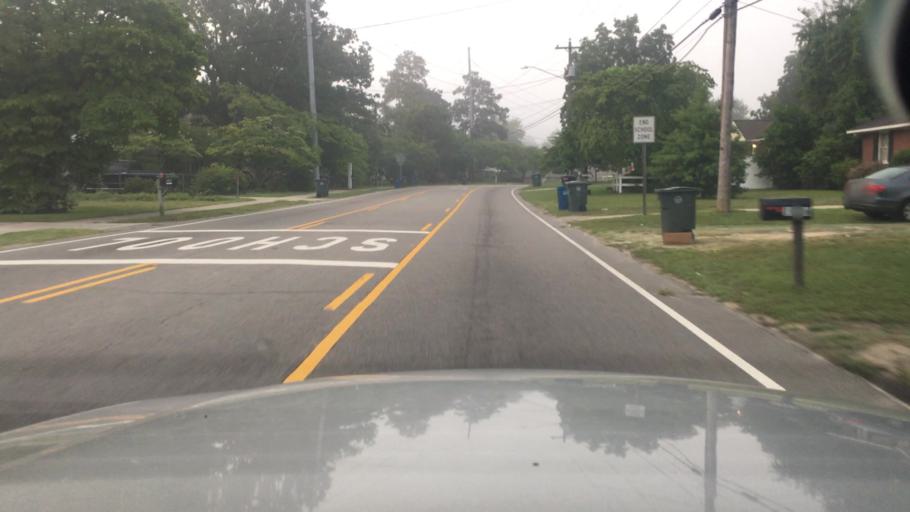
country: US
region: North Carolina
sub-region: Cumberland County
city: Hope Mills
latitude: 35.0227
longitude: -78.9408
